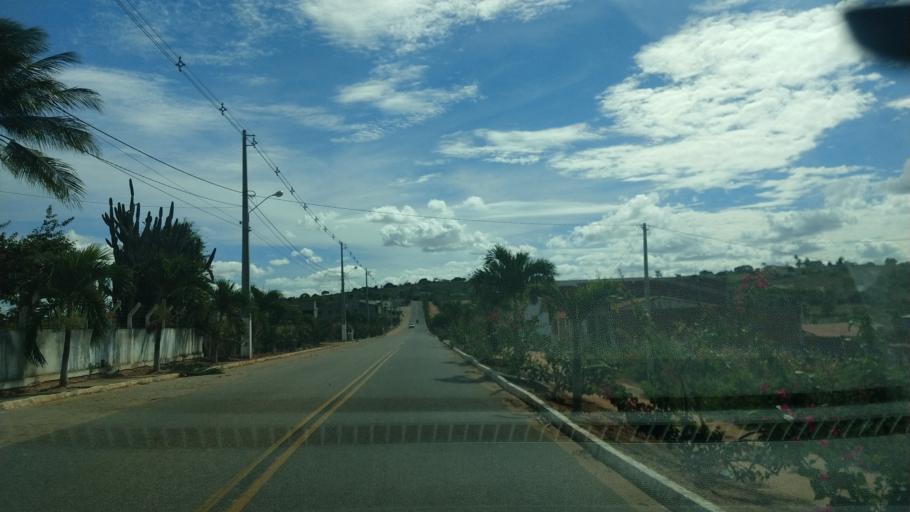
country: BR
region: Rio Grande do Norte
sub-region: Sao Jose Do Campestre
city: Sao Jose do Campestre
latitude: -6.4215
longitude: -35.7120
